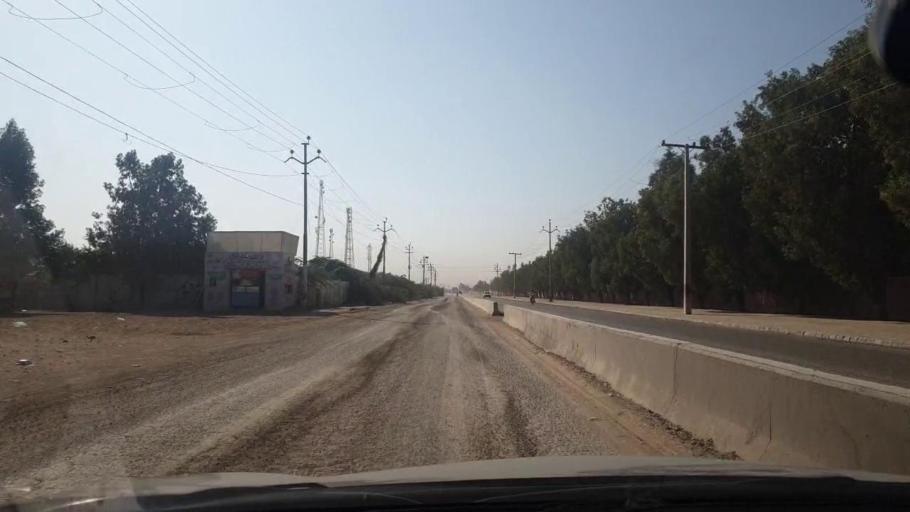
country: PK
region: Sindh
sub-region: Karachi District
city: Karachi
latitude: 25.0825
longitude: 67.0129
